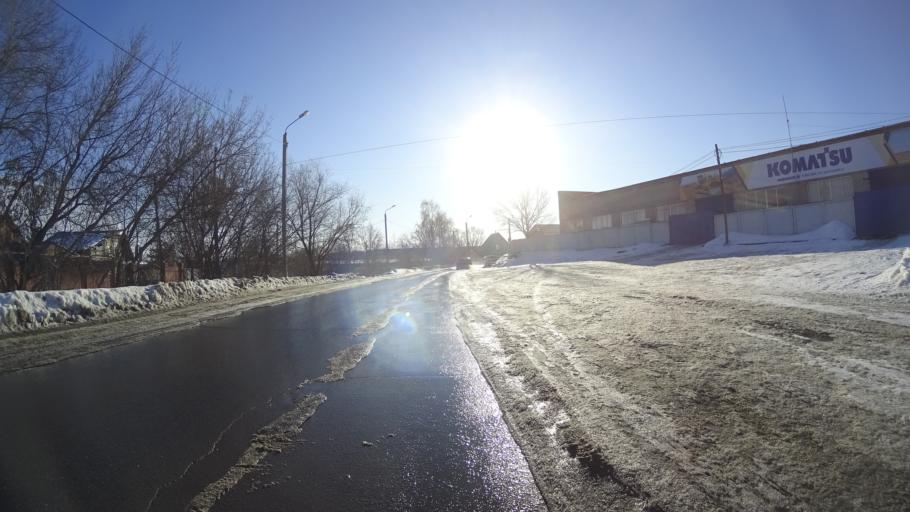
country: RU
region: Chelyabinsk
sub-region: Gorod Chelyabinsk
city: Chelyabinsk
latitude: 55.1491
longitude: 61.3071
